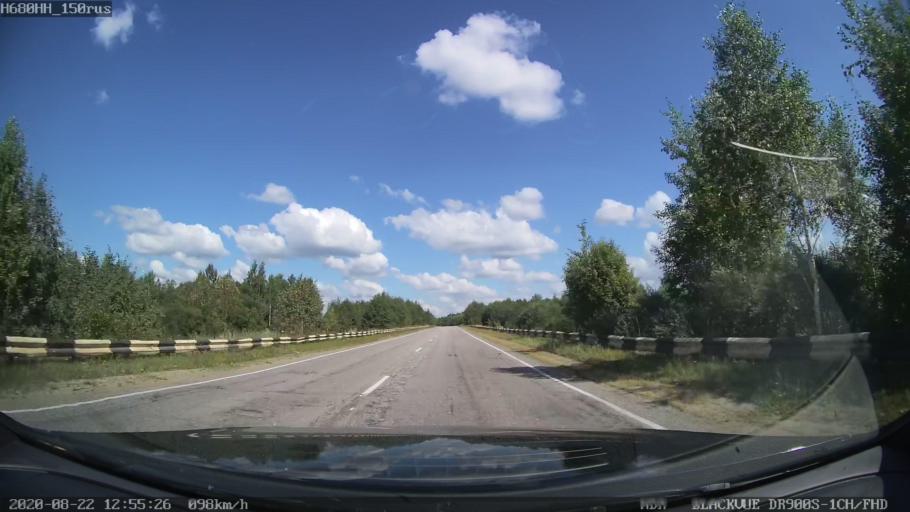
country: RU
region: Tverskaya
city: Rameshki
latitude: 57.5435
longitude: 36.3015
